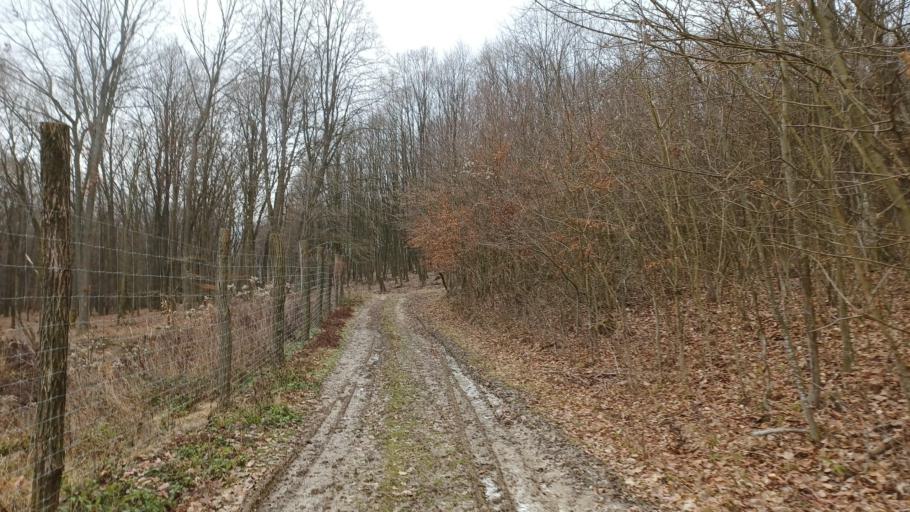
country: HU
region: Tolna
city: Szentgalpuszta
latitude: 46.3085
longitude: 18.6410
